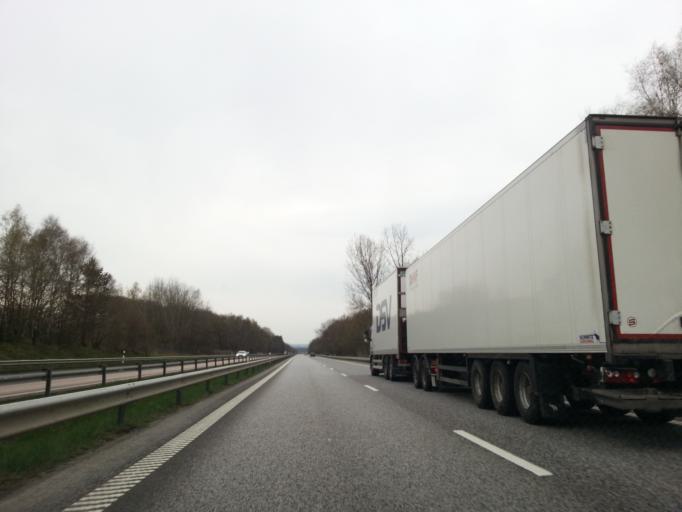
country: SE
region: Skane
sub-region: Bastads Kommun
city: Forslov
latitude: 56.3360
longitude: 12.9146
